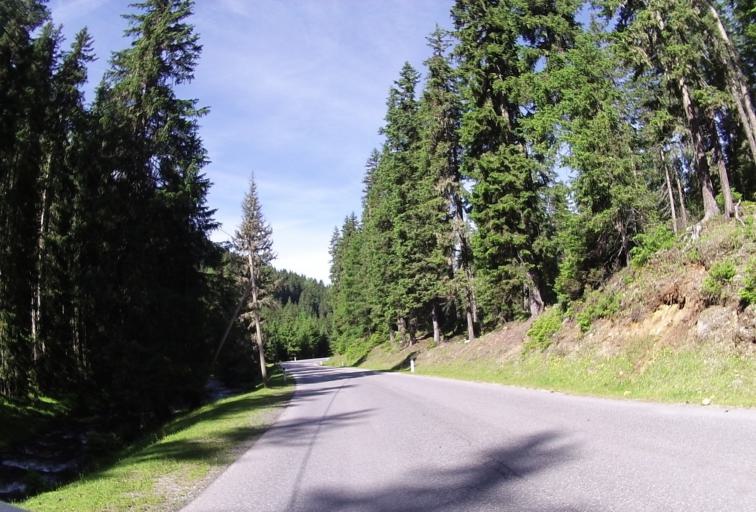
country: AT
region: Tyrol
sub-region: Politischer Bezirk Imst
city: Silz
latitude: 47.2294
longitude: 10.9462
